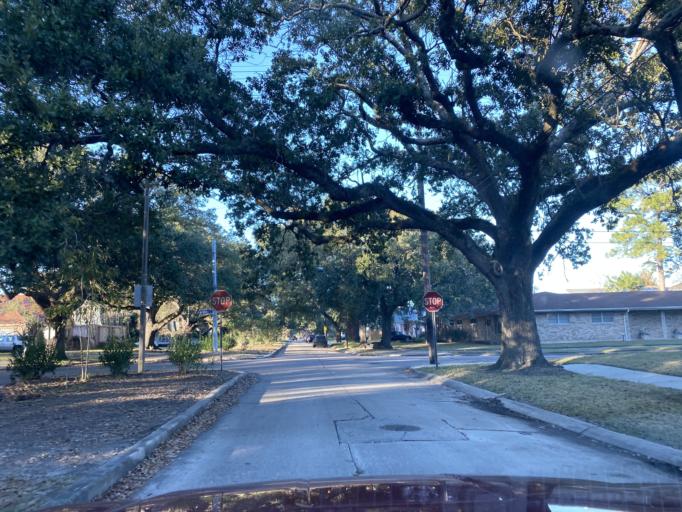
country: US
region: Louisiana
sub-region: Orleans Parish
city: New Orleans
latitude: 30.0082
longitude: -90.0554
